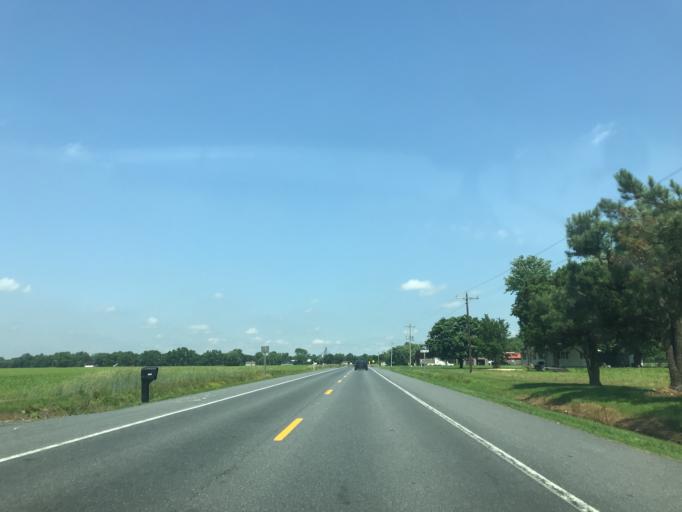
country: US
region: Maryland
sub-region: Caroline County
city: Federalsburg
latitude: 38.6325
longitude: -75.7163
